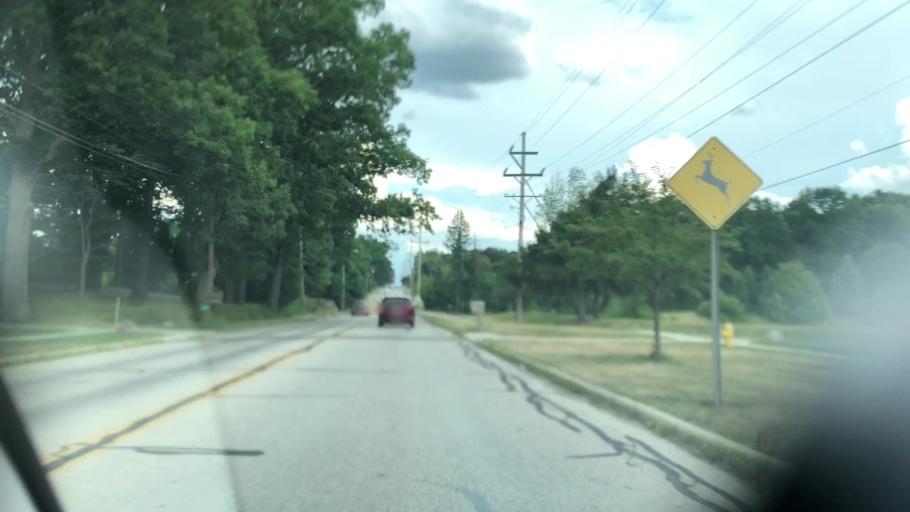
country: US
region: Ohio
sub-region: Summit County
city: Barberton
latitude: 41.0104
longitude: -81.5751
